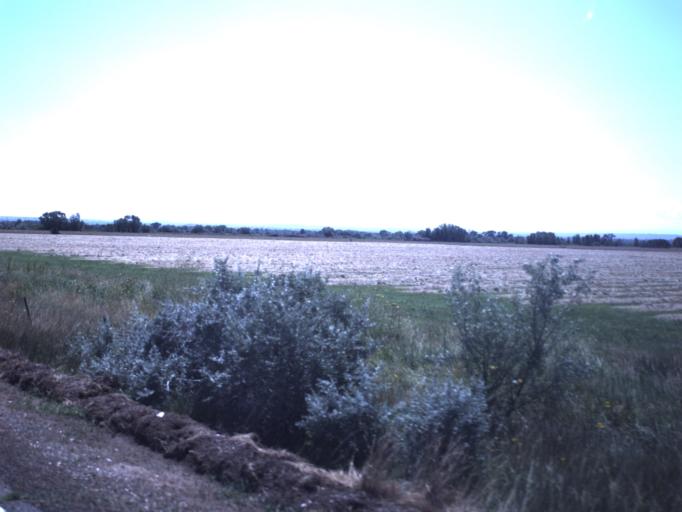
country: US
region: Utah
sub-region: Duchesne County
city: Roosevelt
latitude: 40.4329
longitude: -109.9617
